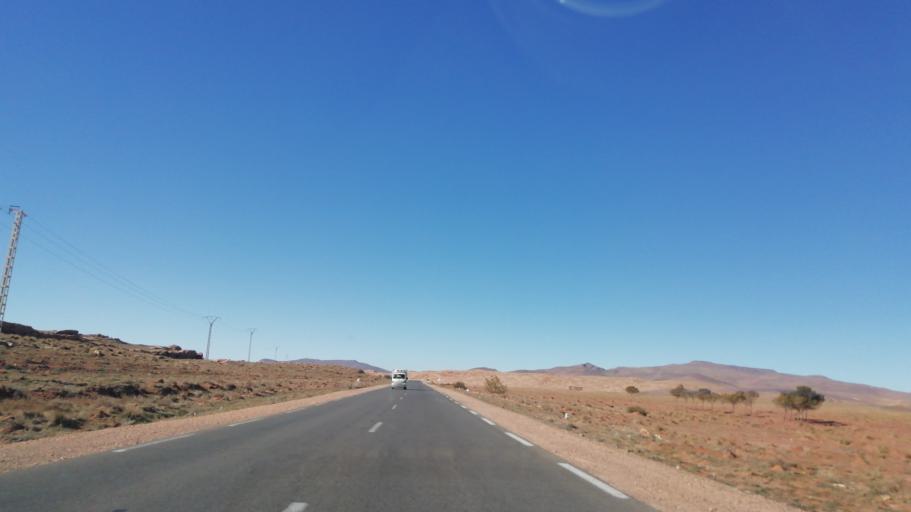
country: DZ
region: El Bayadh
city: El Bayadh
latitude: 33.6167
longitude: 1.2065
